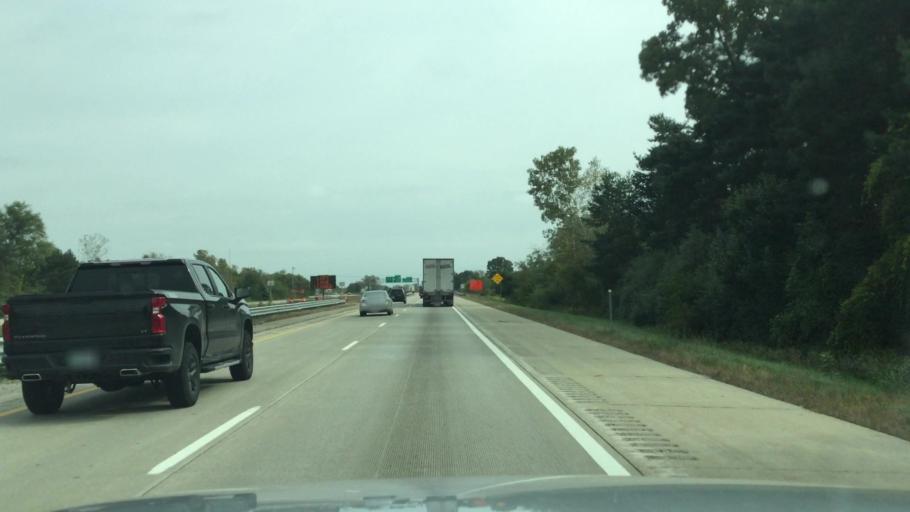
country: US
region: Michigan
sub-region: Genesee County
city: Swartz Creek
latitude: 42.9688
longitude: -83.7759
